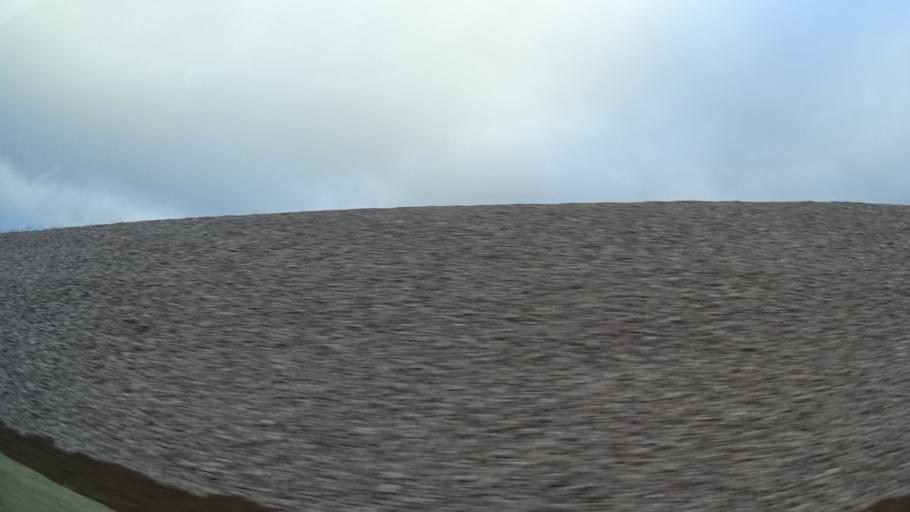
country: DE
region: Thuringia
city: Stadtilm
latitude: 50.7587
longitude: 11.0606
